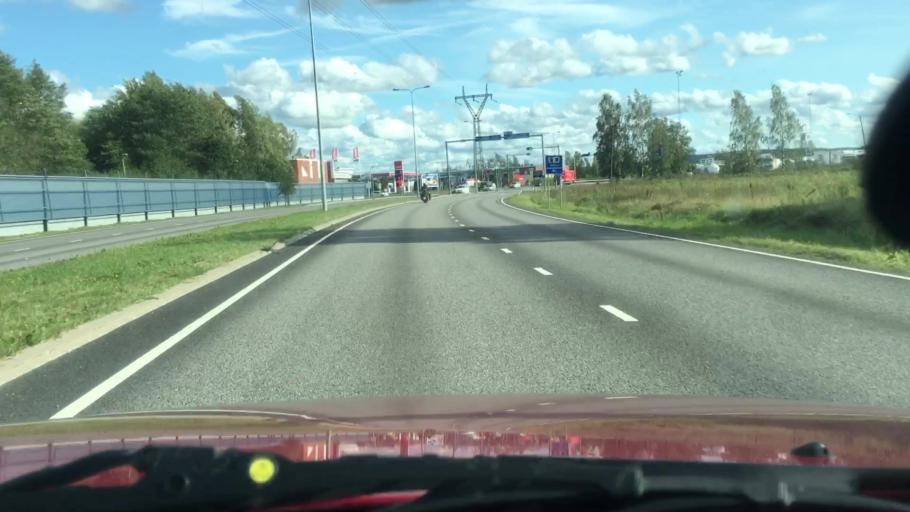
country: FI
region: Varsinais-Suomi
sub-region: Turku
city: Raisio
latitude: 60.4512
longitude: 22.1995
